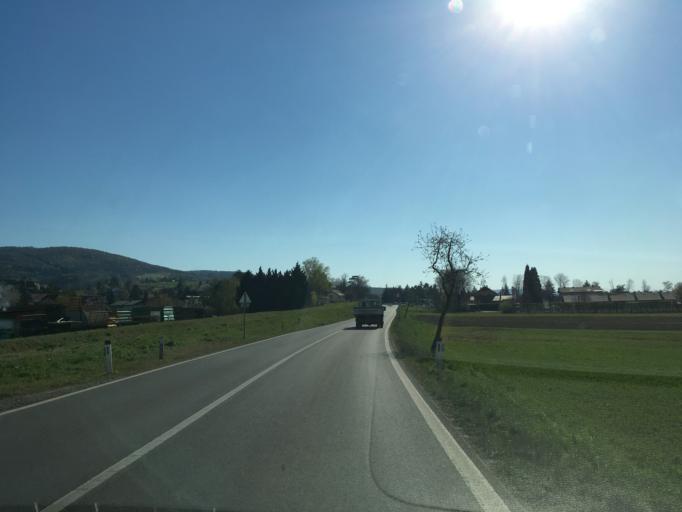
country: AT
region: Lower Austria
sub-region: Politischer Bezirk Tulln
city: Konigstetten
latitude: 48.3077
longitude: 16.1616
